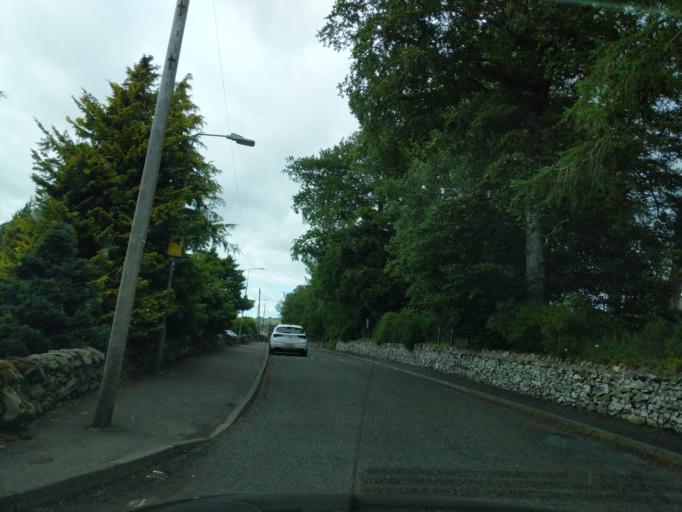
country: GB
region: Scotland
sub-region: The Scottish Borders
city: Peebles
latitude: 55.6446
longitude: -3.1991
